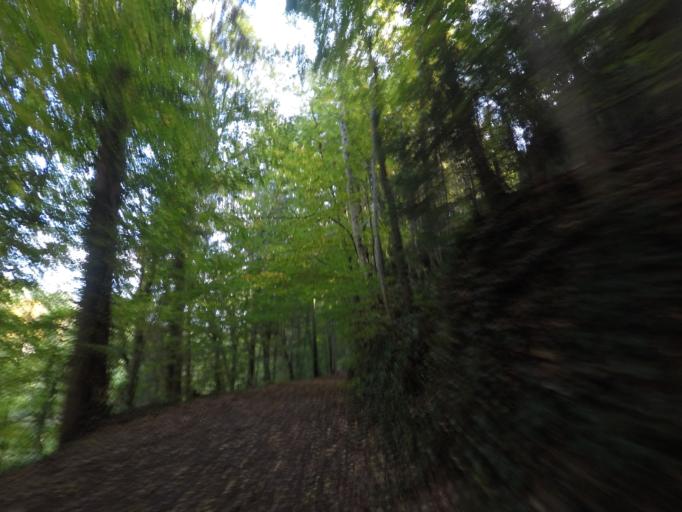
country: LU
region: Luxembourg
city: Kirchberg
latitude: 49.6076
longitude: 6.1633
